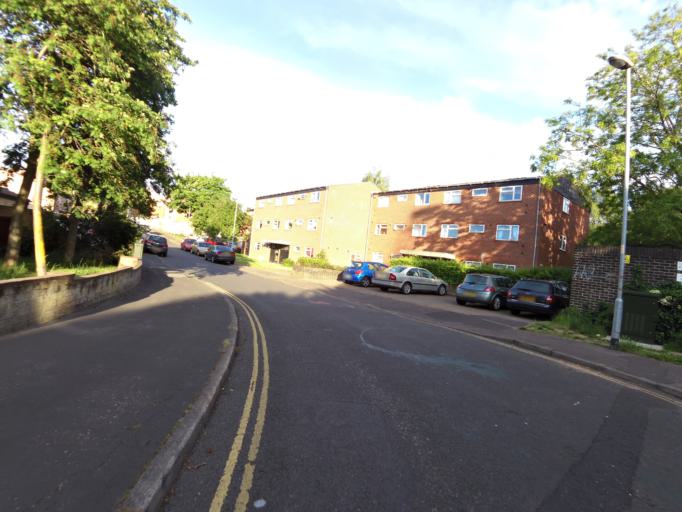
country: GB
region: England
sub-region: Norfolk
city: Norwich
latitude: 52.6605
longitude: 1.2887
